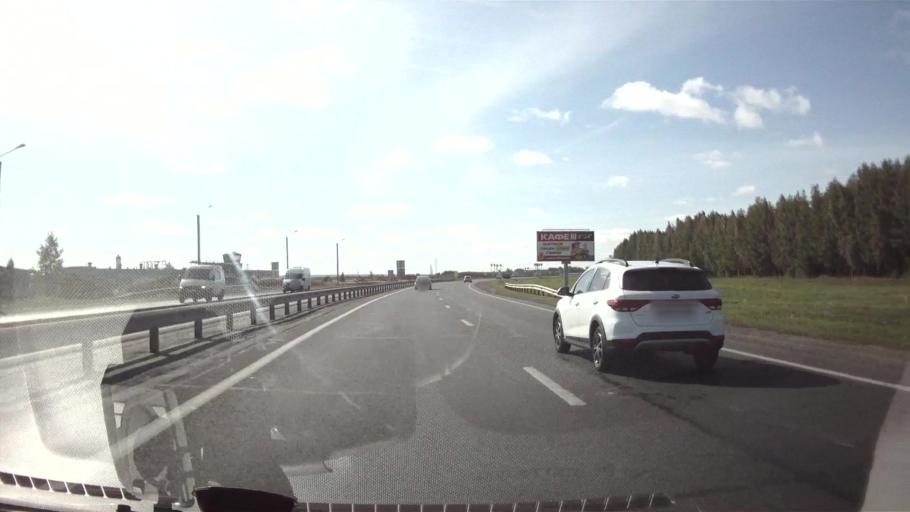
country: RU
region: Ulyanovsk
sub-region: Ulyanovskiy Rayon
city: Ulyanovsk
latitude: 54.2741
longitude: 48.2612
